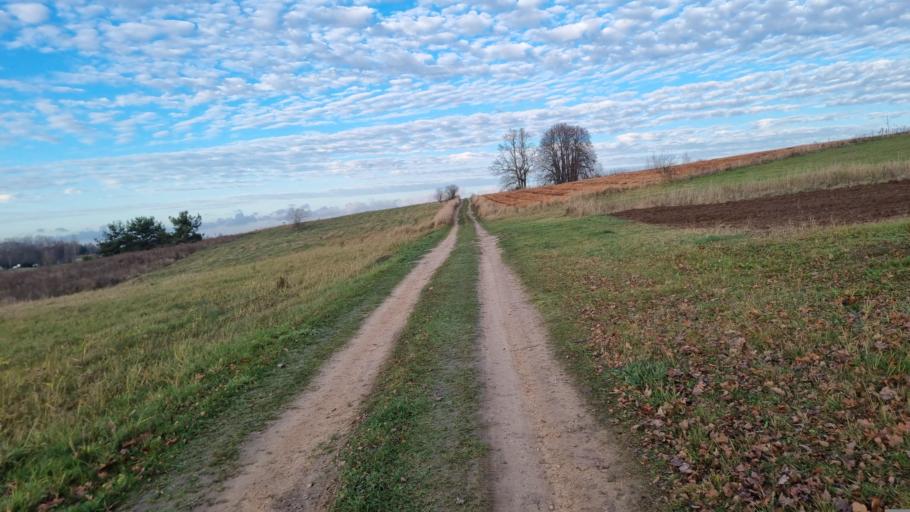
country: LV
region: Kekava
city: Kekava
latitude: 56.7874
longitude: 24.2486
